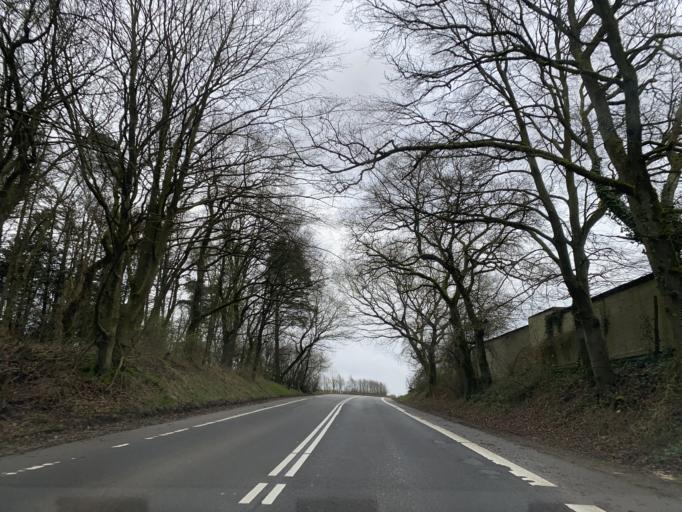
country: DK
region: Central Jutland
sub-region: Viborg Kommune
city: Bjerringbro
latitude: 56.2981
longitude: 9.5996
